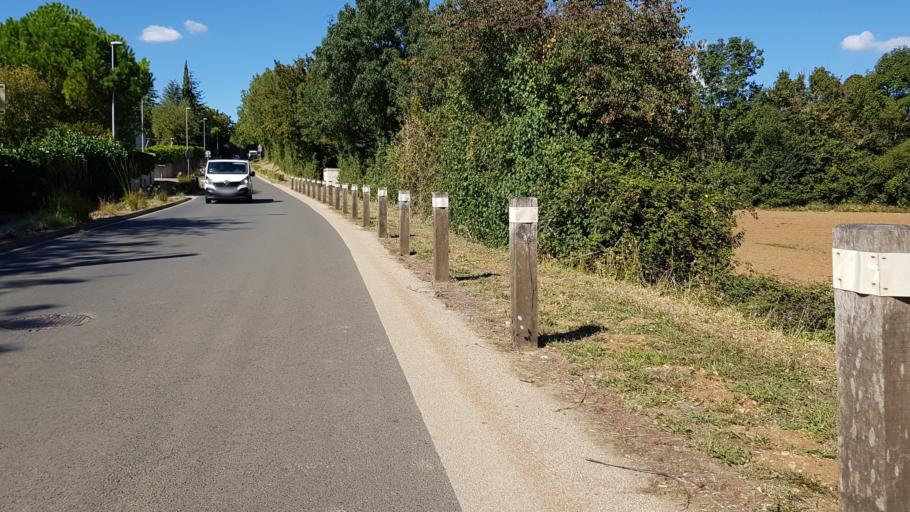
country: FR
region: Poitou-Charentes
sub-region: Departement des Deux-Sevres
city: Vouille
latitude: 46.3189
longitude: -0.3695
